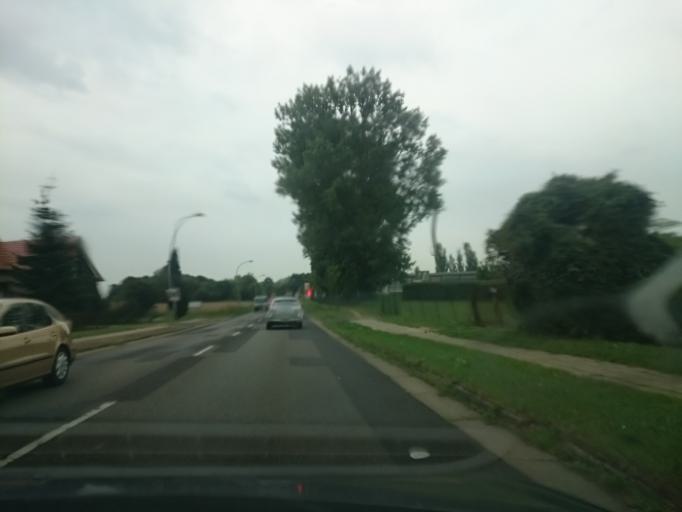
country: DE
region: Brandenburg
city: Gransee
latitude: 53.0007
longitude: 13.1574
